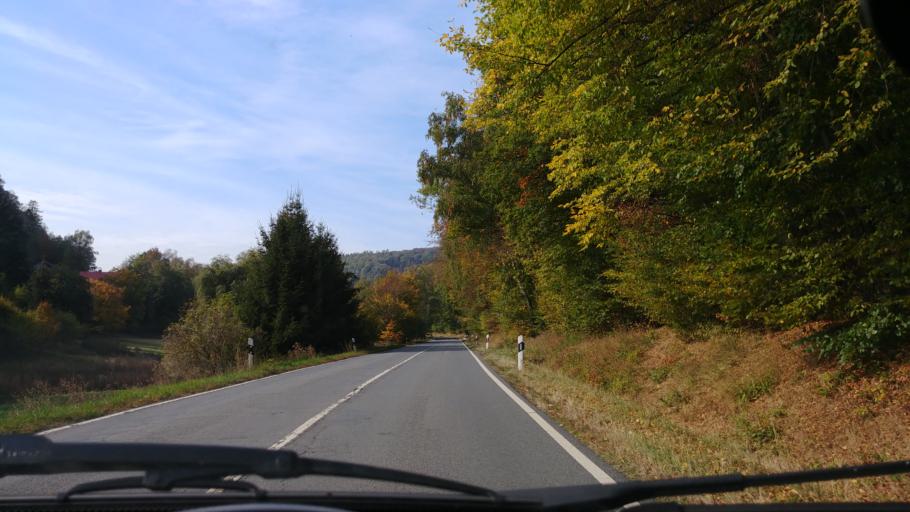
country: DE
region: Hesse
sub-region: Regierungsbezirk Darmstadt
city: Idstein
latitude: 50.1750
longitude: 8.2646
